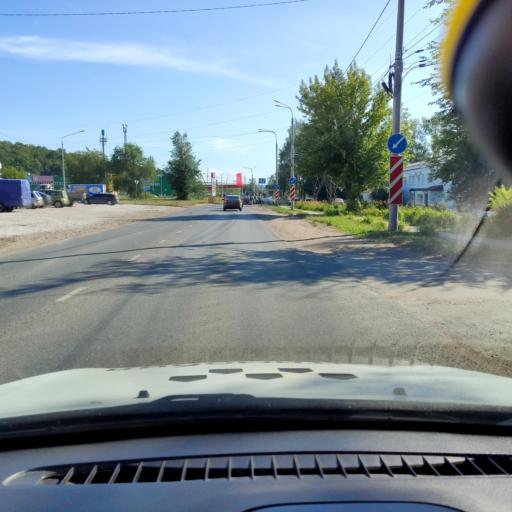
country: RU
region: Samara
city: Zhigulevsk
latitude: 53.4037
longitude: 49.5205
